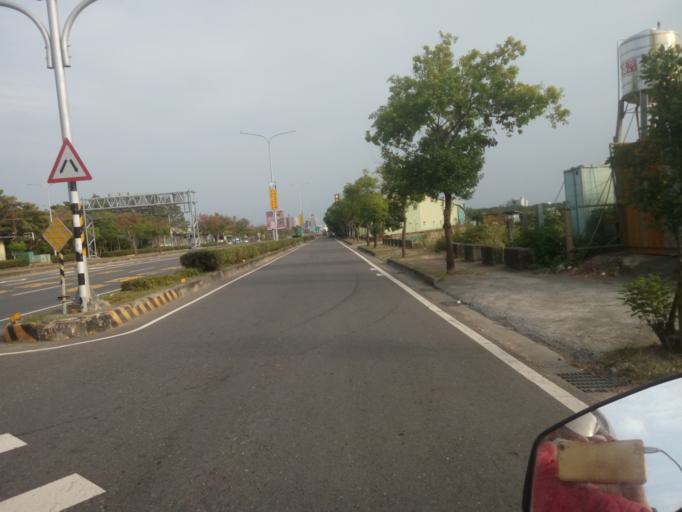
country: TW
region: Taiwan
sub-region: Chiayi
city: Jiayi Shi
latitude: 23.4837
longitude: 120.4139
